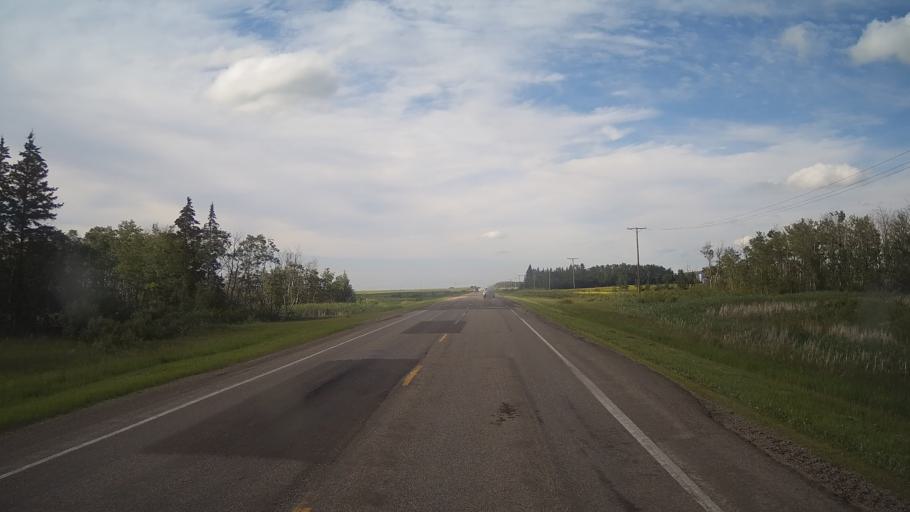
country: CA
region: Saskatchewan
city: Foam Lake
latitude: 51.6015
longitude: -103.8459
